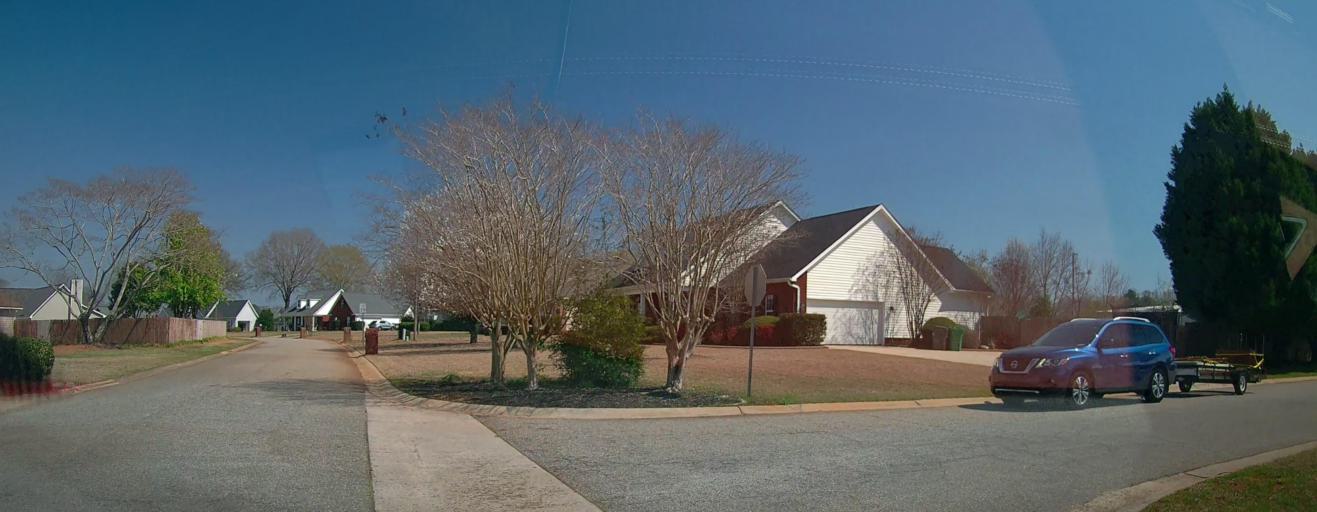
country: US
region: Georgia
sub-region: Houston County
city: Centerville
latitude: 32.5816
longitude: -83.7116
